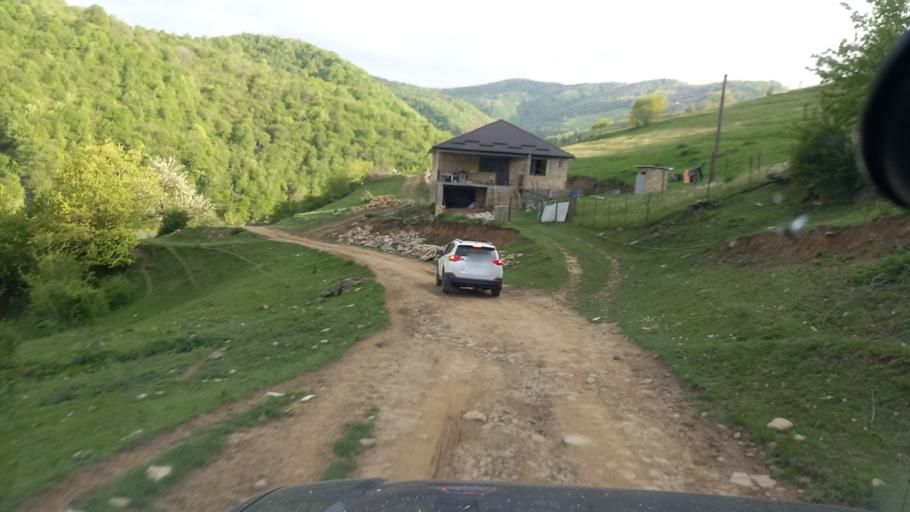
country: RU
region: Dagestan
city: Khuchni
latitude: 41.9473
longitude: 47.8339
